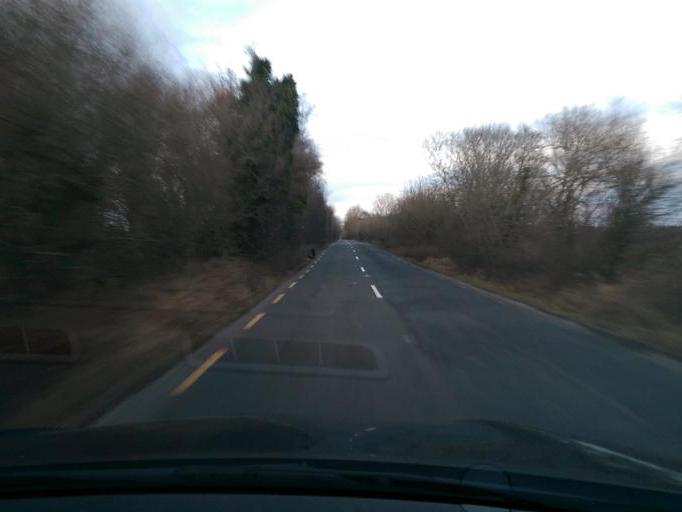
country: IE
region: Connaught
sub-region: County Galway
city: Portumna
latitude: 53.0641
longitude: -8.0901
